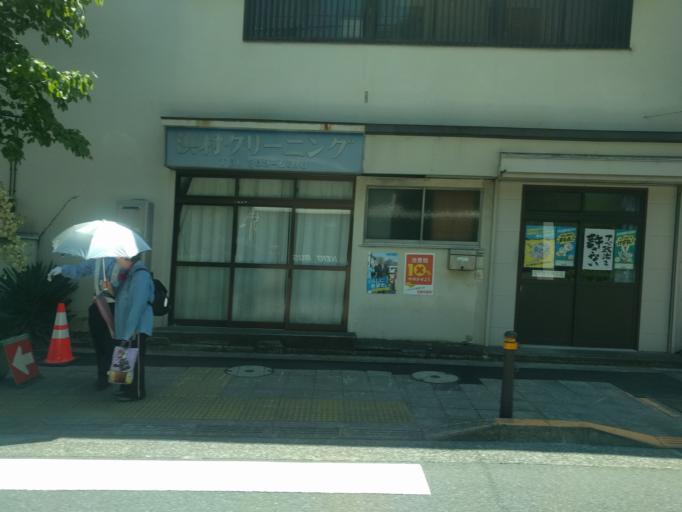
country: JP
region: Tokyo
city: Mitaka-shi
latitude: 35.6636
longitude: 139.6210
